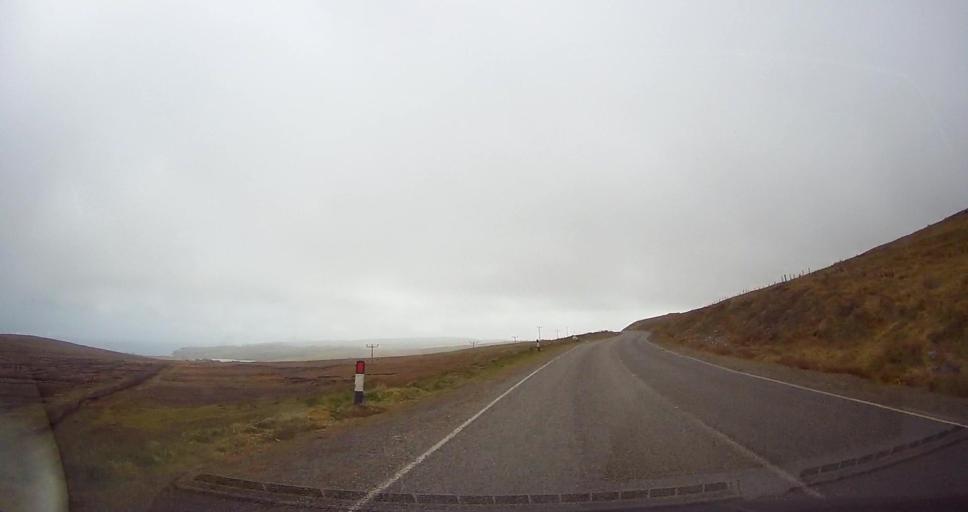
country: GB
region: Scotland
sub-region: Shetland Islands
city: Sandwick
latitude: 59.9600
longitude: -1.2841
